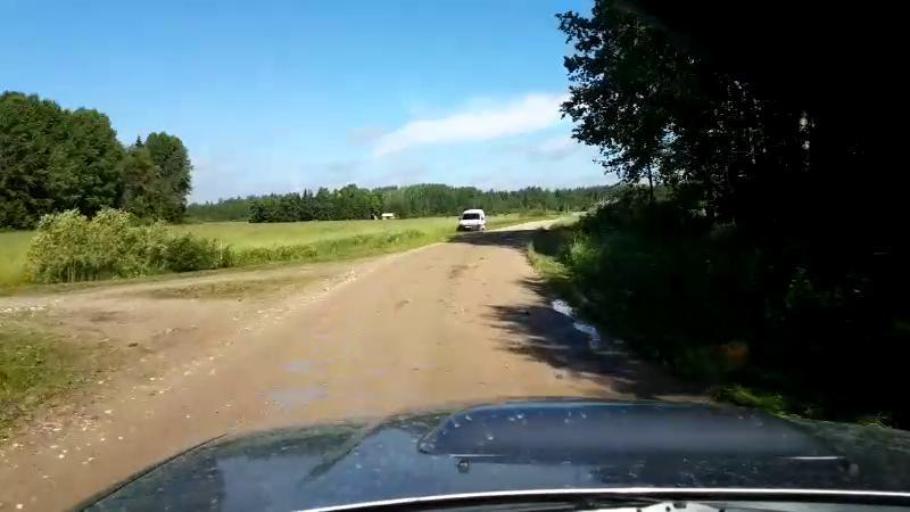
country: EE
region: Paernumaa
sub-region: Sindi linn
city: Sindi
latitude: 58.5214
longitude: 24.6488
